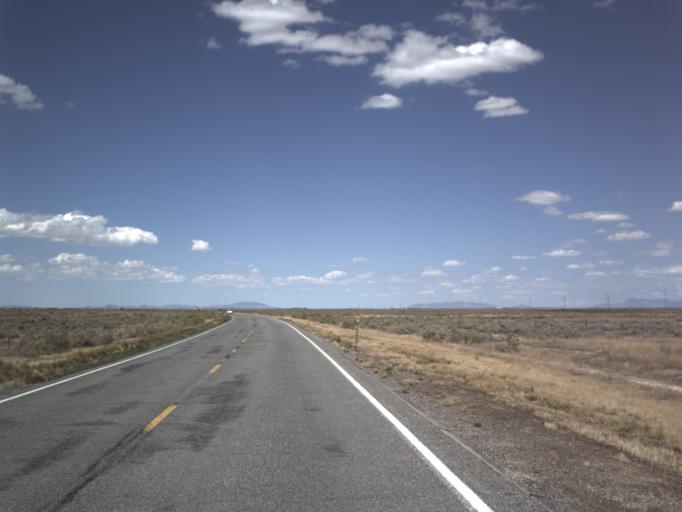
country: US
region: Utah
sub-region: Millard County
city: Delta
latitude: 39.2547
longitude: -112.4420
